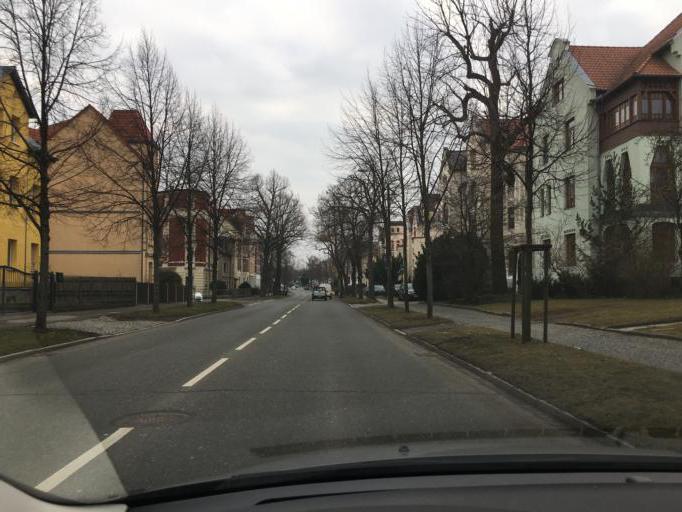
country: DE
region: Thuringia
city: Altenburg
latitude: 50.9853
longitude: 12.4469
